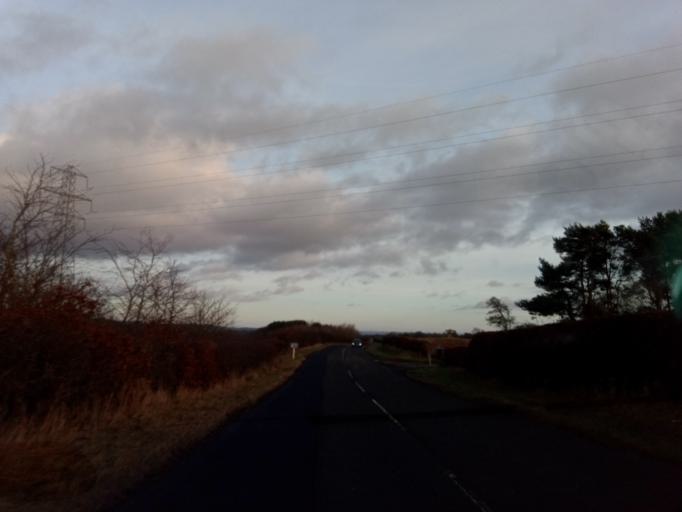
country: GB
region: Scotland
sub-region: The Scottish Borders
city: Melrose
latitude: 55.5517
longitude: -2.7519
